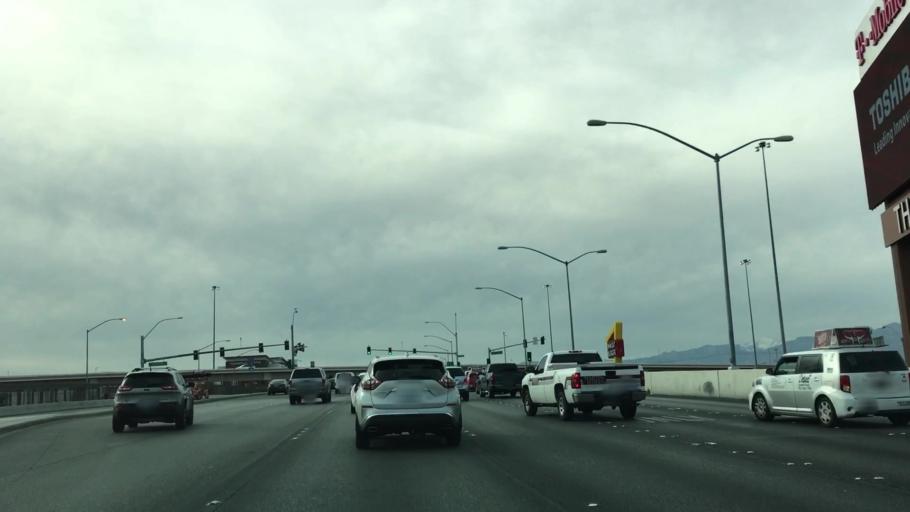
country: US
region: Nevada
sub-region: Clark County
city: Paradise
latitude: 36.1009
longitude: -115.1784
